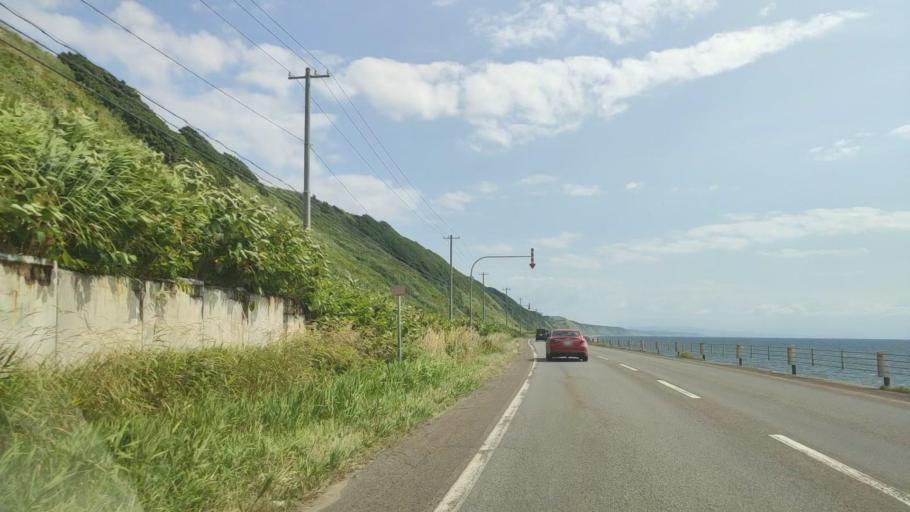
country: JP
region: Hokkaido
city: Rumoi
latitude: 44.0911
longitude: 141.6610
